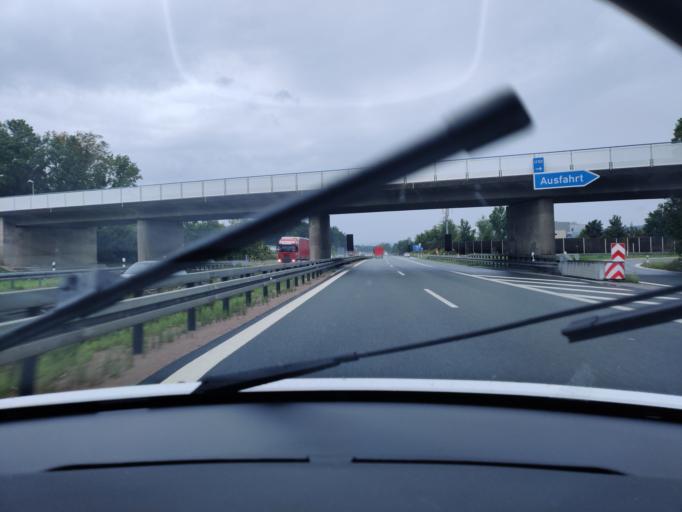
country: DE
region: Bavaria
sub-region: Upper Palatinate
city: Pfreimd
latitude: 49.4912
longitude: 12.1890
